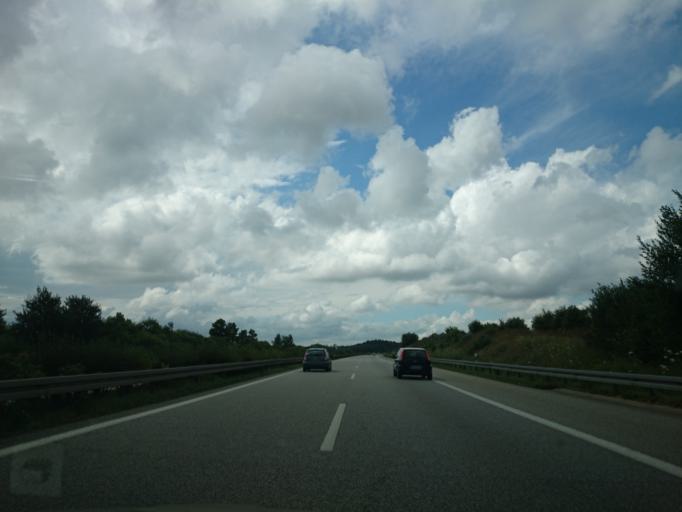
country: DE
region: Mecklenburg-Vorpommern
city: Ludersdorf
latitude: 53.9233
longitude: 11.8018
